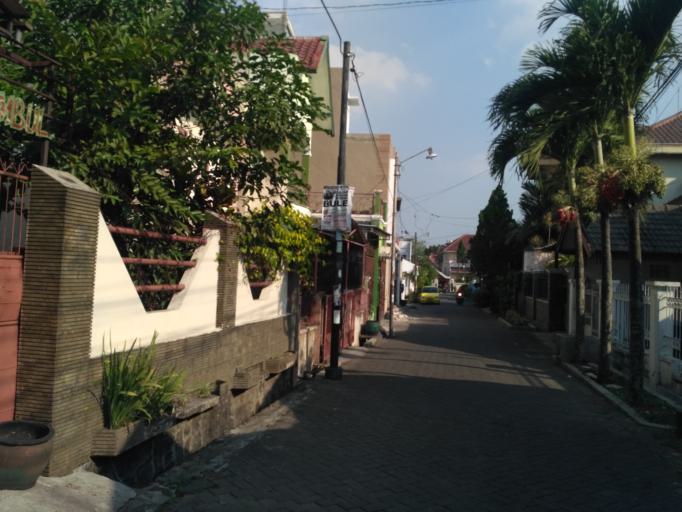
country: ID
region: East Java
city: Malang
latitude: -7.9562
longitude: 112.6098
